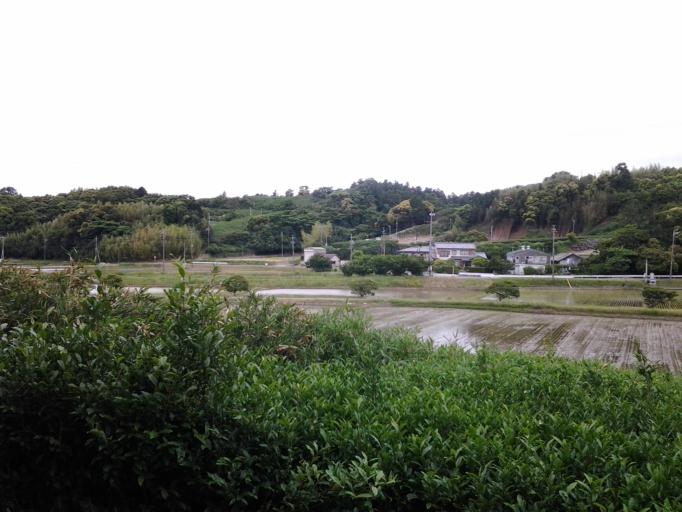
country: JP
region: Shizuoka
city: Sagara
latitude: 34.6838
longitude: 138.1219
